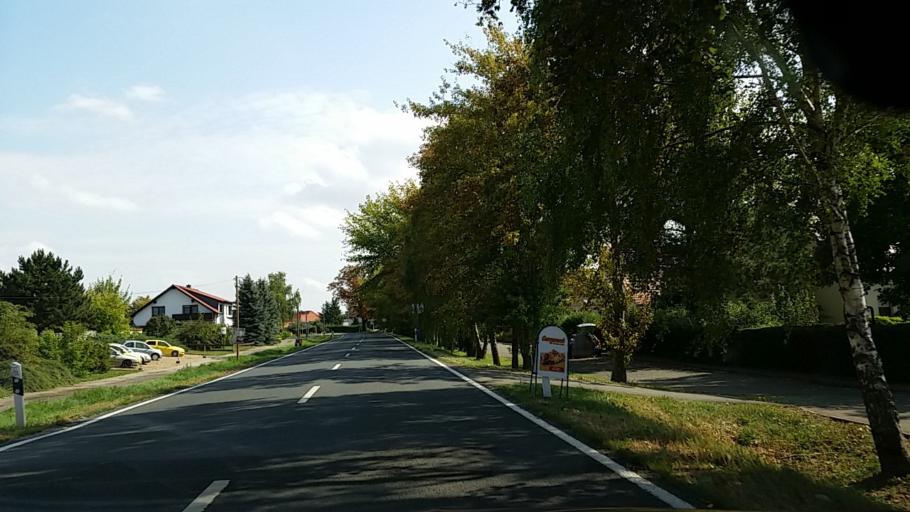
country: DE
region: Thuringia
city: Oldisleben
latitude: 51.3468
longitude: 11.1714
